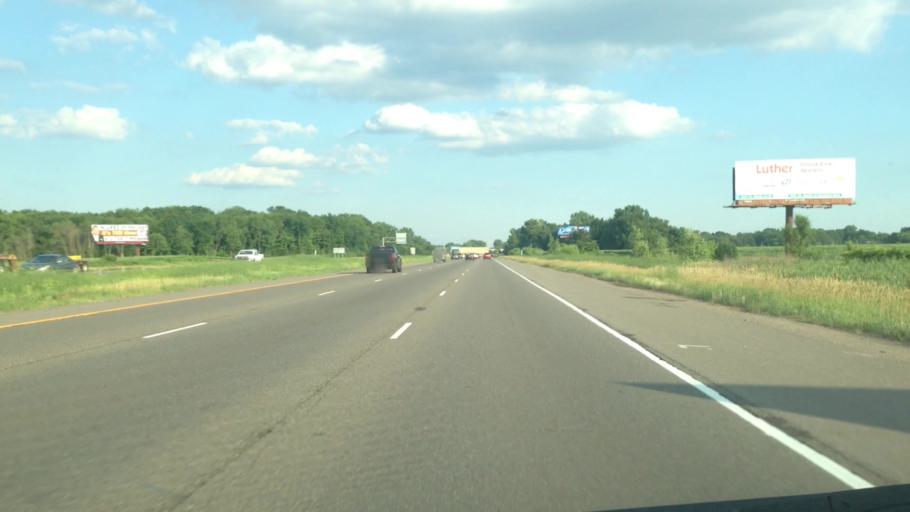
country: US
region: Minnesota
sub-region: Hennepin County
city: Rogers
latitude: 45.1827
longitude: -93.5358
